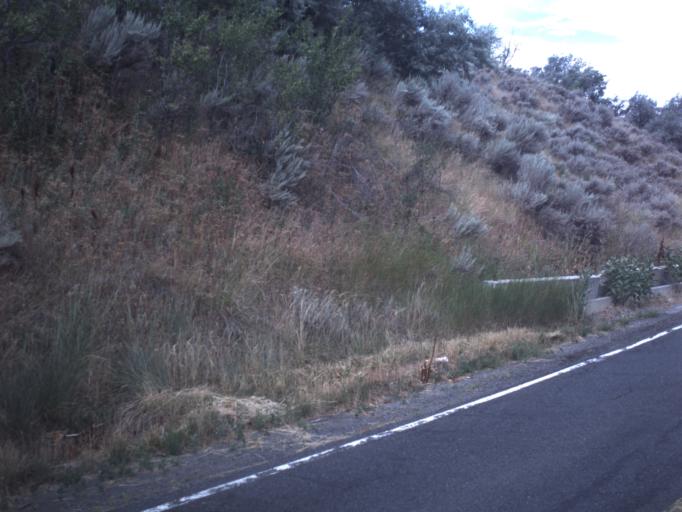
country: US
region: Utah
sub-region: Weber County
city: Washington Terrace
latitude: 41.1492
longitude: -111.9822
